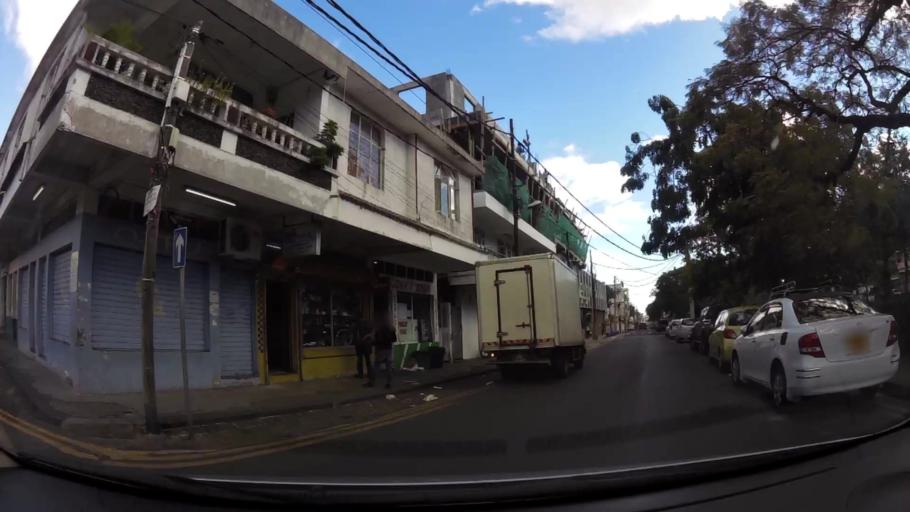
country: MU
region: Port Louis
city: Port Louis
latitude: -20.1629
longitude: 57.5152
